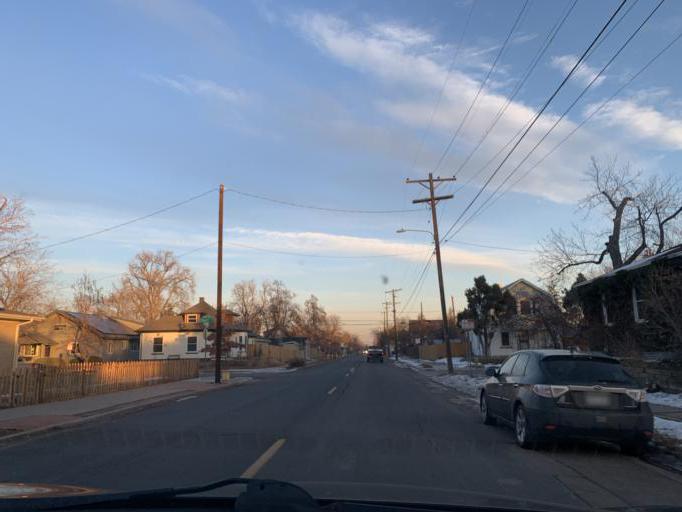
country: US
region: Colorado
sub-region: Adams County
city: Berkley
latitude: 39.7874
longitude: -105.0432
